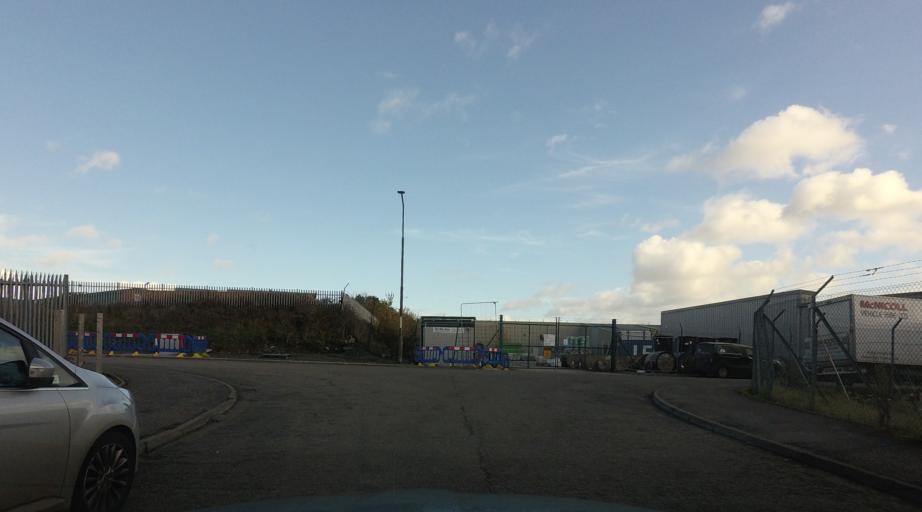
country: GB
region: Scotland
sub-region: West Lothian
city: Broxburn
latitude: 55.9423
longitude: -3.4543
